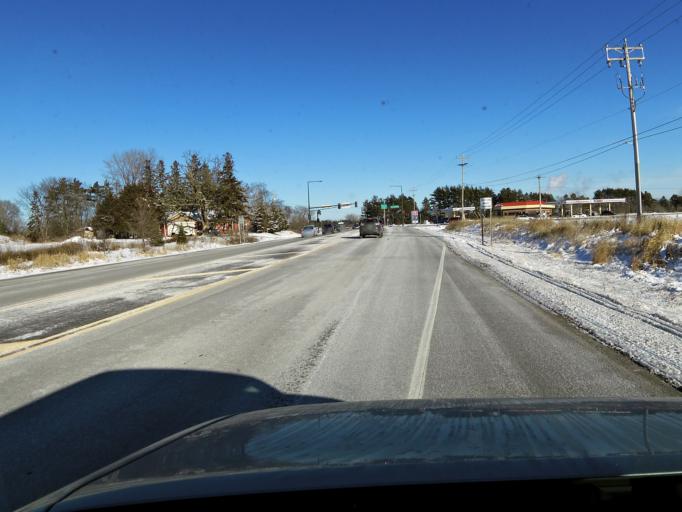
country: US
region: Minnesota
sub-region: Washington County
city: Lake Elmo
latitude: 45.0092
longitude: -92.8660
